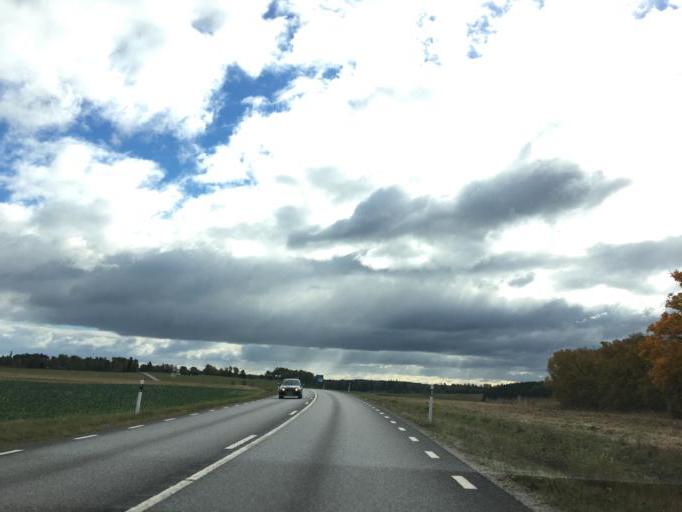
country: SE
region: Soedermanland
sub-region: Katrineholms Kommun
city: Katrineholm
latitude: 58.9541
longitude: 16.3697
